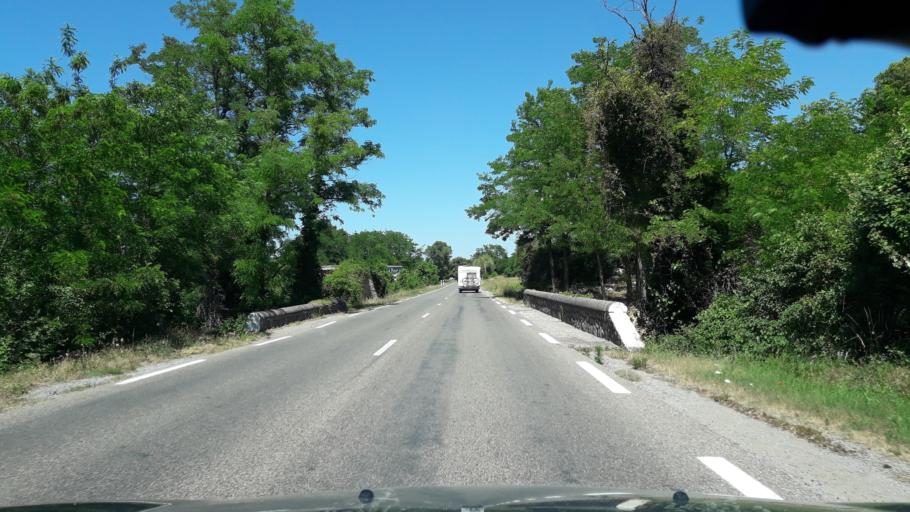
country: FR
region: Rhone-Alpes
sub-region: Departement de l'Ardeche
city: Ruoms
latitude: 44.4143
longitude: 4.3043
